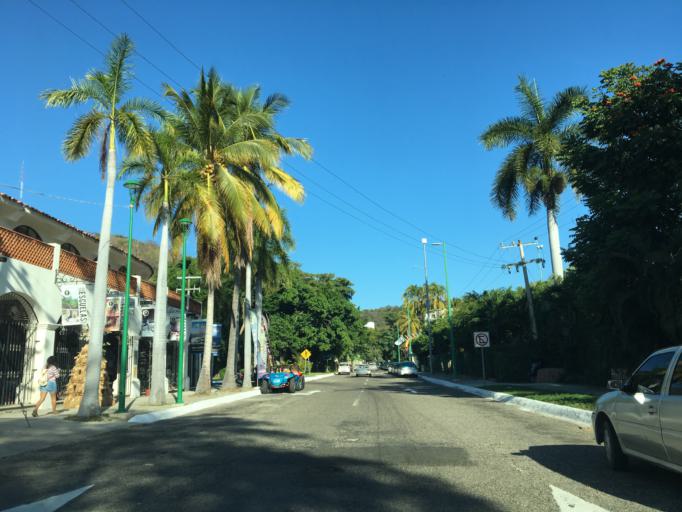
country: MX
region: Oaxaca
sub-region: Santa Maria Huatulco
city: Crucecita
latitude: 15.7747
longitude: -96.0966
